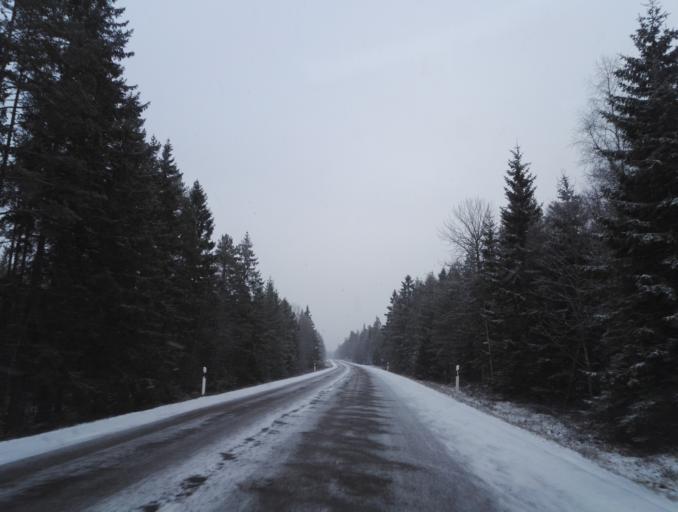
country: SE
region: Kronoberg
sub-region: Uppvidinge Kommun
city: Lenhovda
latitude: 56.8930
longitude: 15.3713
